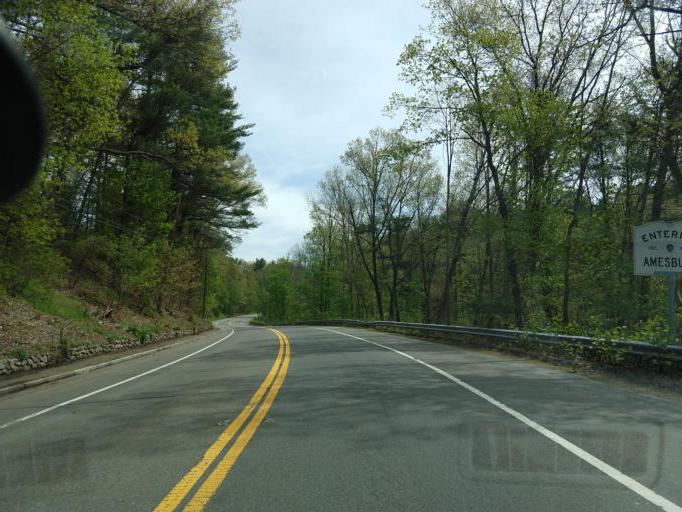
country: US
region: Massachusetts
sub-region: Essex County
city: Merrimac
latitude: 42.8383
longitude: -70.9767
